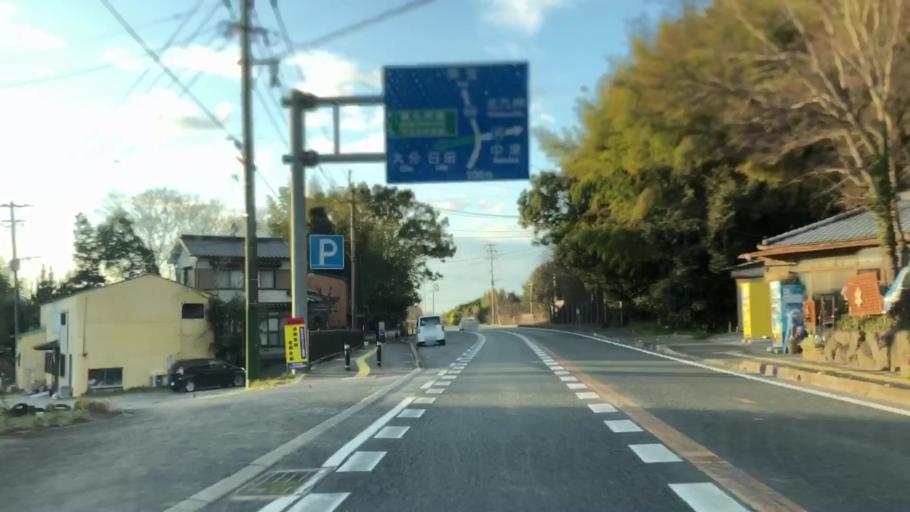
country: JP
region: Fukuoka
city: Nakatsu
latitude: 33.5383
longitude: 131.2992
